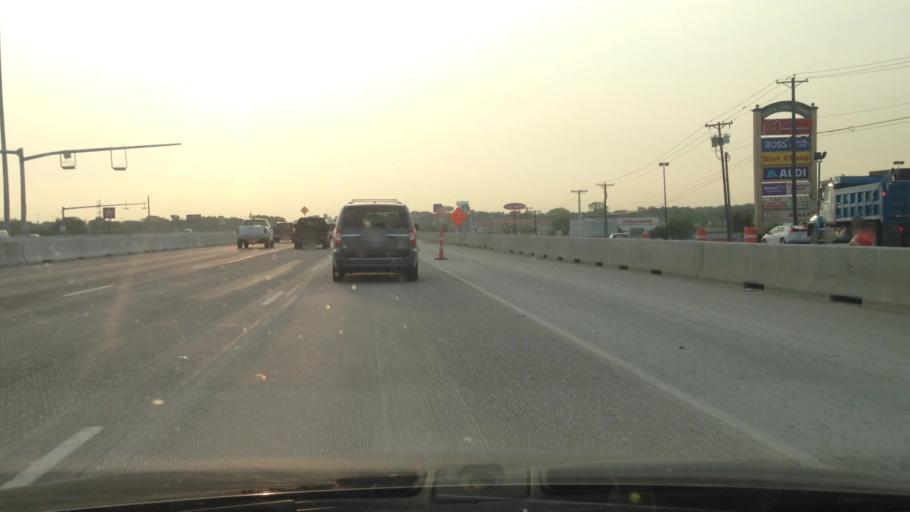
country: US
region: Texas
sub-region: Tarrant County
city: Euless
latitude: 32.8372
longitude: -97.1031
